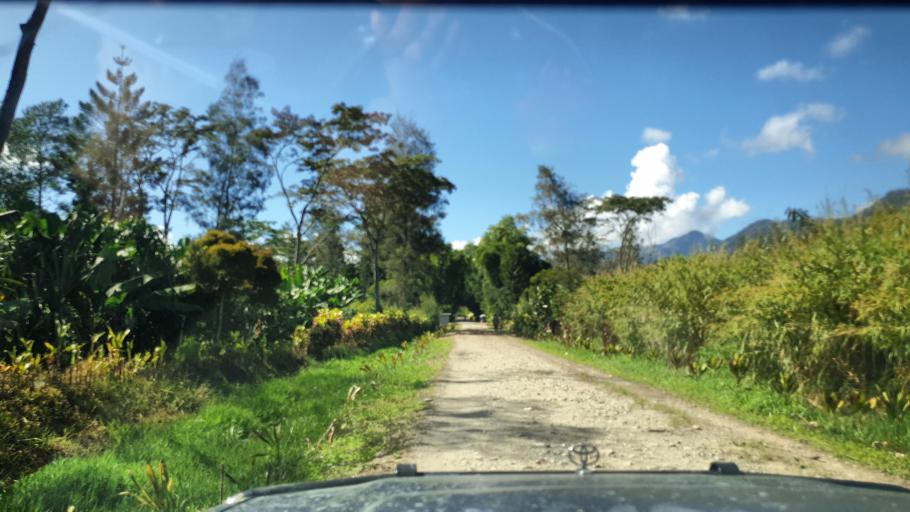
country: PG
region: Western Highlands
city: Rauna
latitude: -5.8192
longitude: 144.3829
